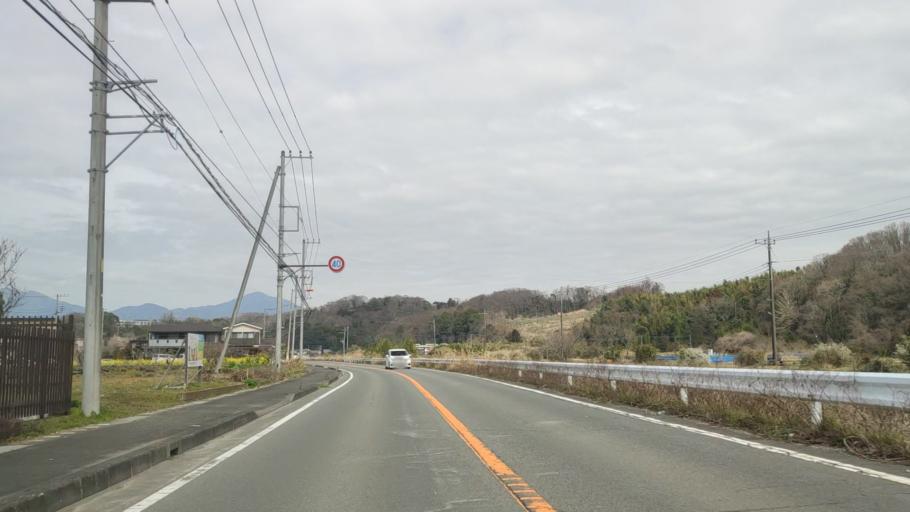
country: JP
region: Kanagawa
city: Ninomiya
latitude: 35.3249
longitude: 139.2189
